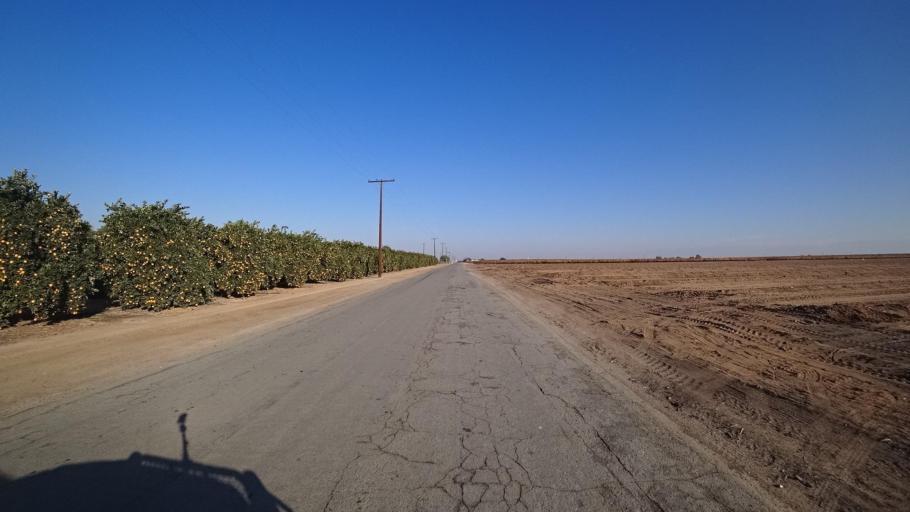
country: US
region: California
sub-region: Tulare County
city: Richgrove
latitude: 35.7669
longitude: -119.1518
